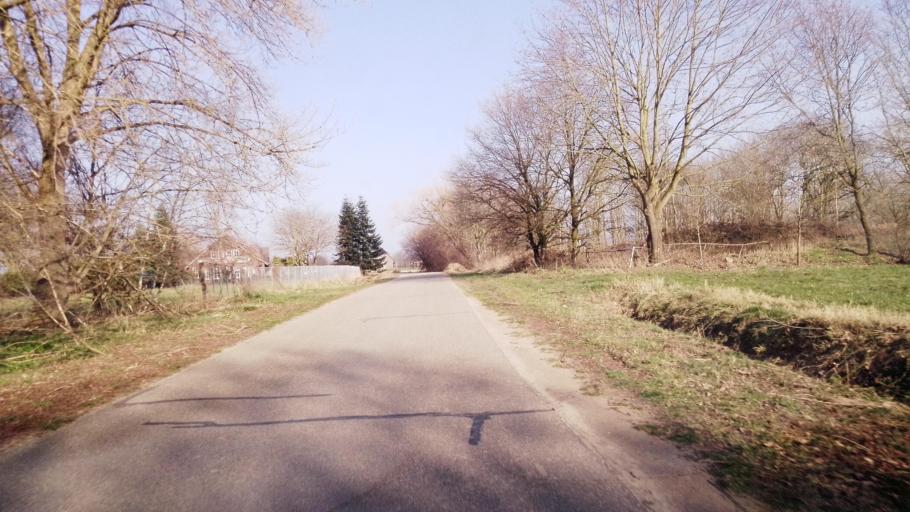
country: NL
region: Limburg
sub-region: Gemeente Beesel
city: Reuver
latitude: 51.2998
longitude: 6.0734
